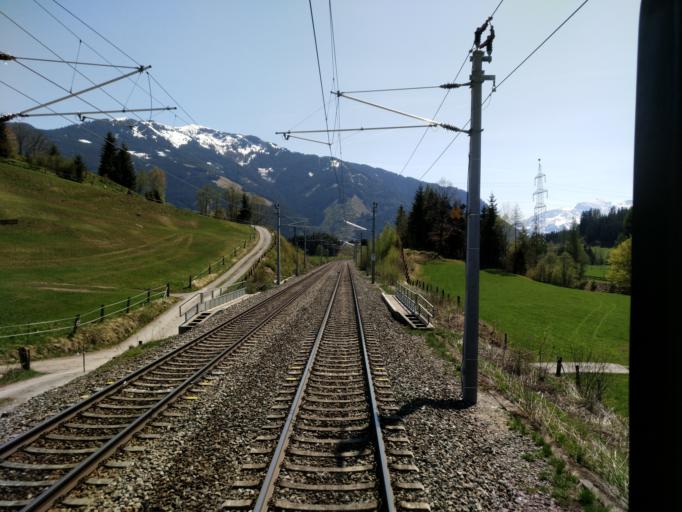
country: AT
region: Salzburg
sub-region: Politischer Bezirk Zell am See
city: Saalfelden am Steinernen Meer
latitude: 47.4070
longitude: 12.8285
